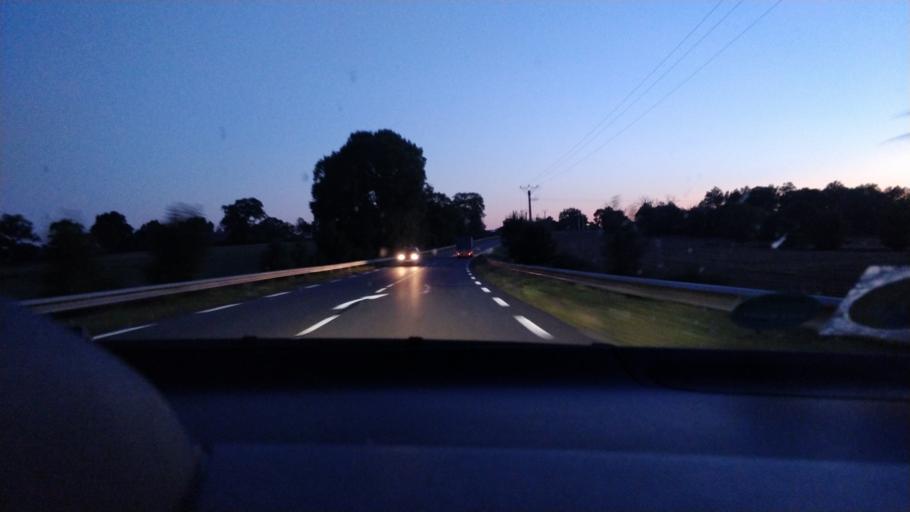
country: FR
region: Poitou-Charentes
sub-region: Departement de la Charente
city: Chasseneuil-sur-Bonnieure
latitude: 45.8408
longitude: 0.4896
